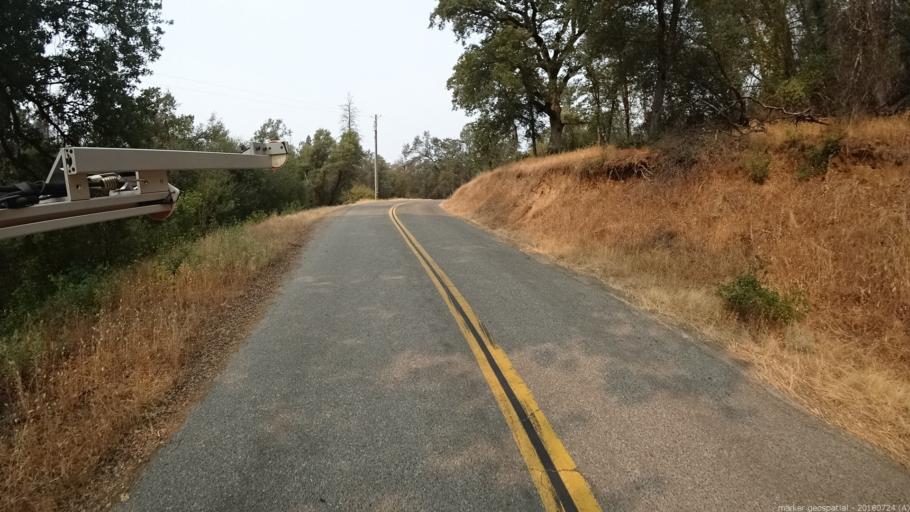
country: US
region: California
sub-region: Madera County
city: Oakhurst
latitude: 37.3358
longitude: -119.6092
